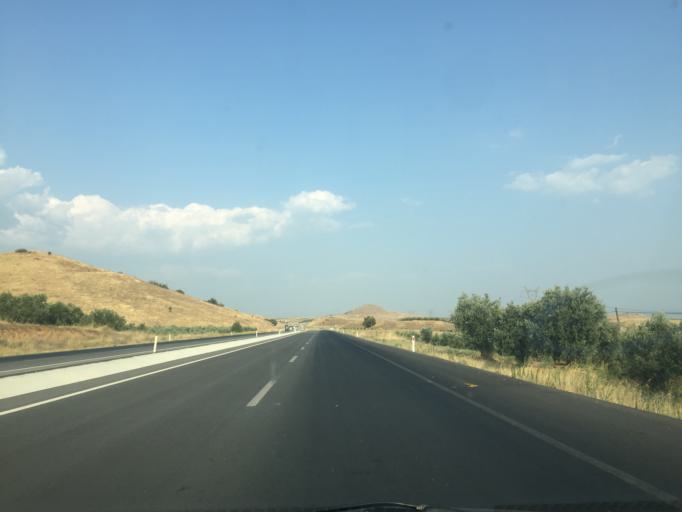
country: TR
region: Manisa
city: Ahmetli
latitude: 38.5829
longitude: 27.9797
